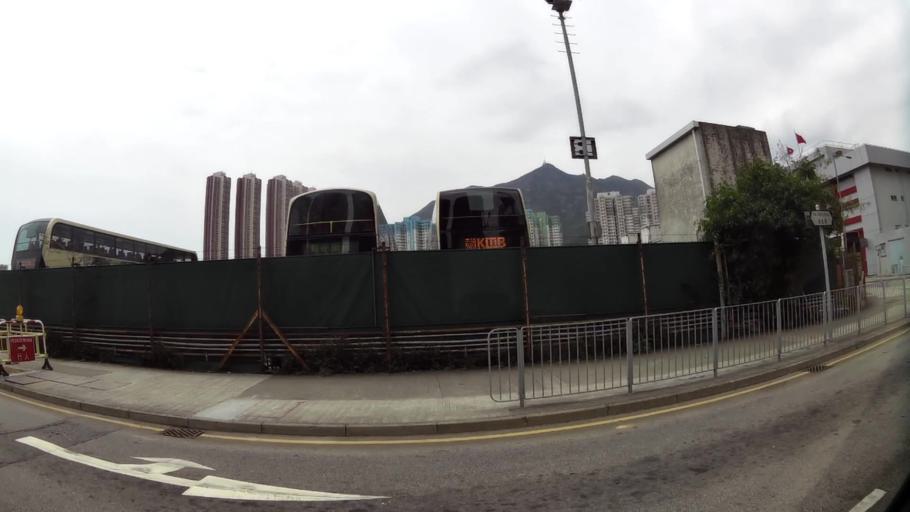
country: HK
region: Tuen Mun
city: Tuen Mun
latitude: 22.3824
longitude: 113.9702
